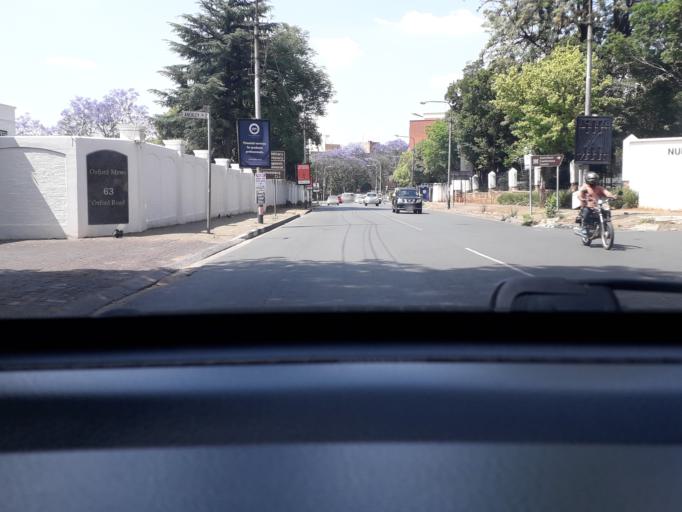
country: ZA
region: Gauteng
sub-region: City of Johannesburg Metropolitan Municipality
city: Johannesburg
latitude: -26.1662
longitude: 28.0468
